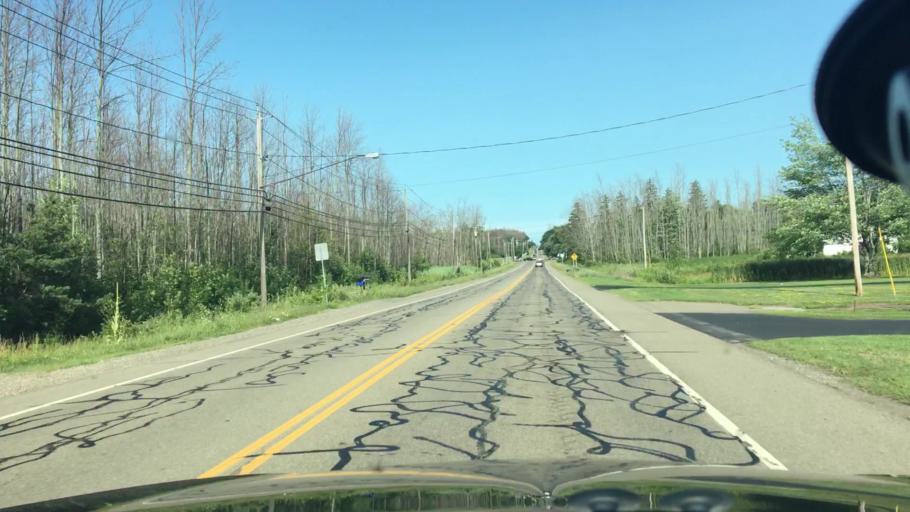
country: US
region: New York
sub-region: Erie County
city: Angola
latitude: 42.6525
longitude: -78.9867
